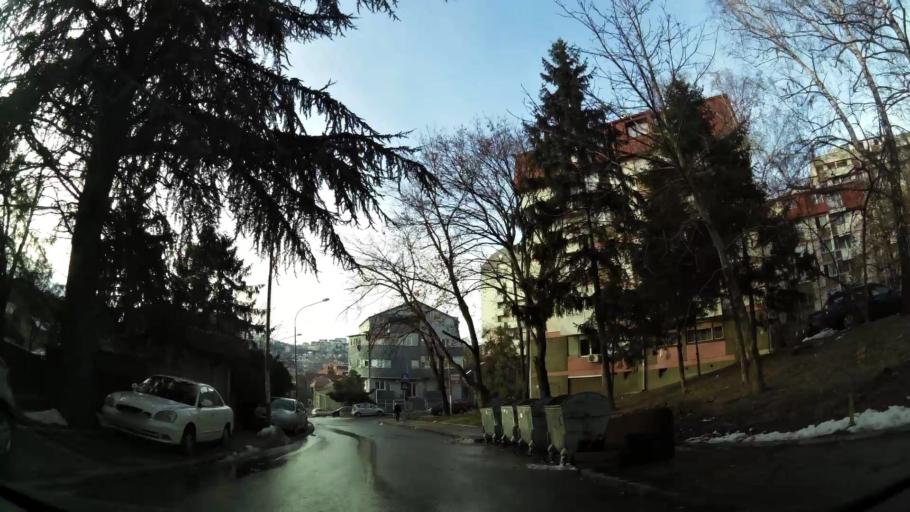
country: RS
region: Central Serbia
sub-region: Belgrade
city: Rakovica
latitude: 44.7455
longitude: 20.4507
